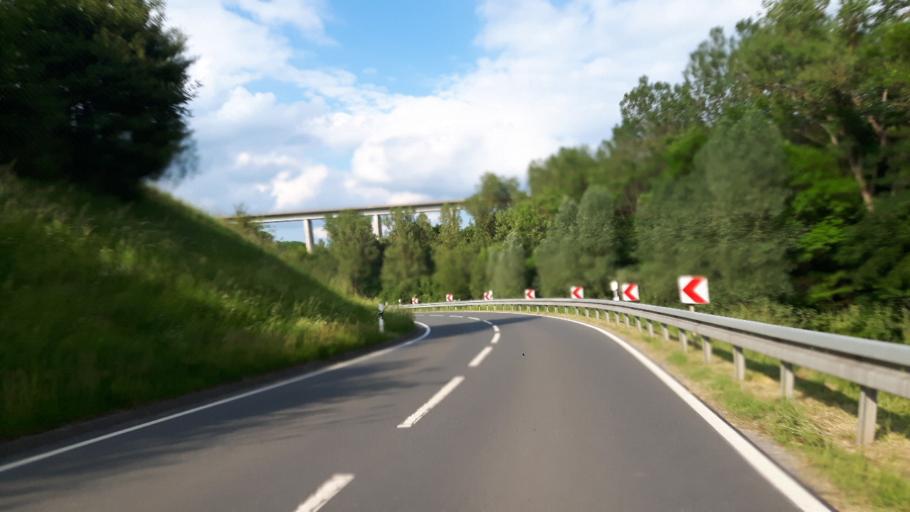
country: DE
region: Bavaria
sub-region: Regierungsbezirk Unterfranken
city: Reichenberg
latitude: 49.7409
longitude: 9.9241
